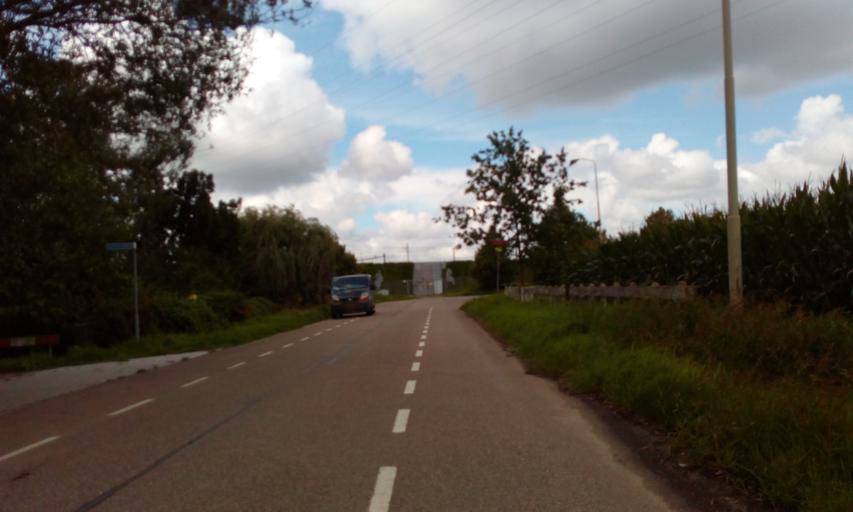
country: NL
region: South Holland
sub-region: Gemeente Barendrecht
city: Barendrecht
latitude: 51.8679
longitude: 4.5428
